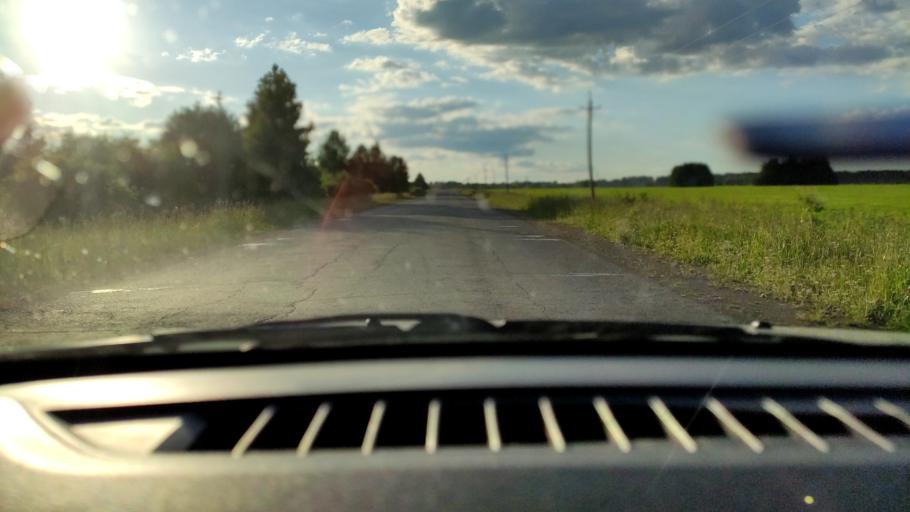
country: RU
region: Perm
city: Uinskoye
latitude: 57.0965
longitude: 56.5475
